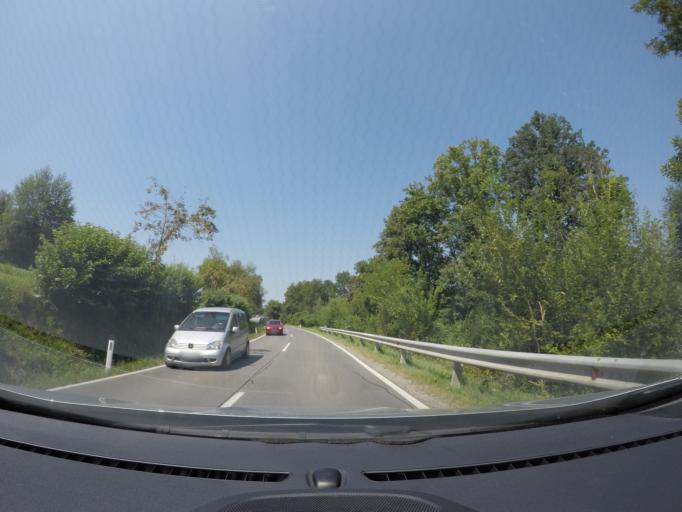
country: AT
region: Lower Austria
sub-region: Politischer Bezirk Sankt Polten
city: Maria-Anzbach
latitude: 48.1865
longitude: 15.9506
